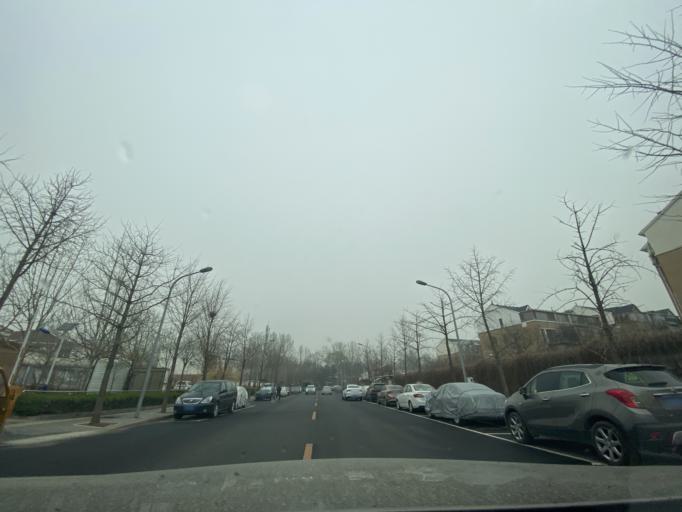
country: CN
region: Beijing
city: Sijiqing
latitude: 39.9573
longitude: 116.2284
